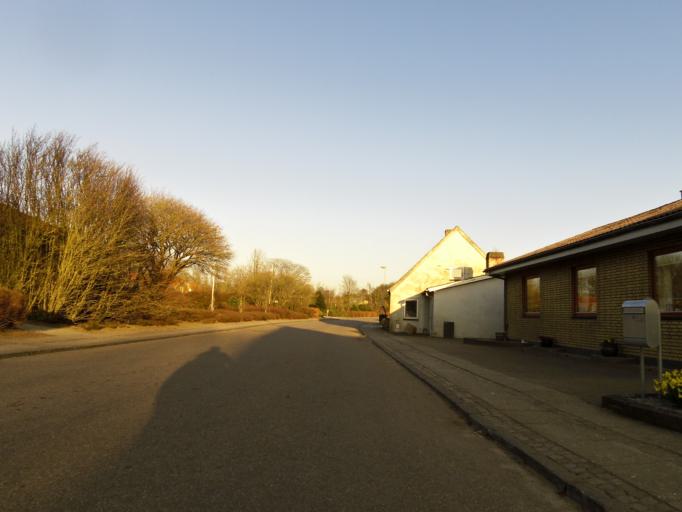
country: DK
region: Central Jutland
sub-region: Holstebro Kommune
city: Vinderup
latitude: 56.5214
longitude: 8.7852
